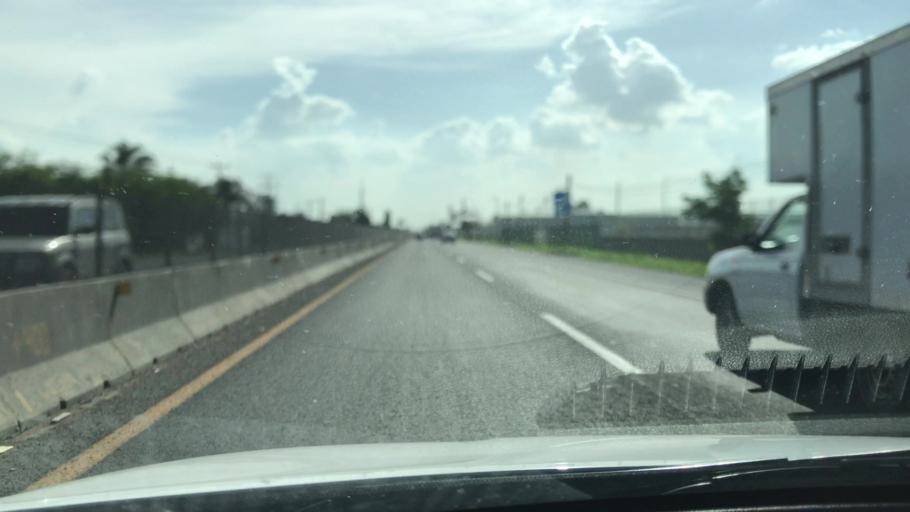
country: MX
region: Guanajuato
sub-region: Cortazar
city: Colonia la Calzada (La Olla)
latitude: 20.5120
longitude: -100.9425
